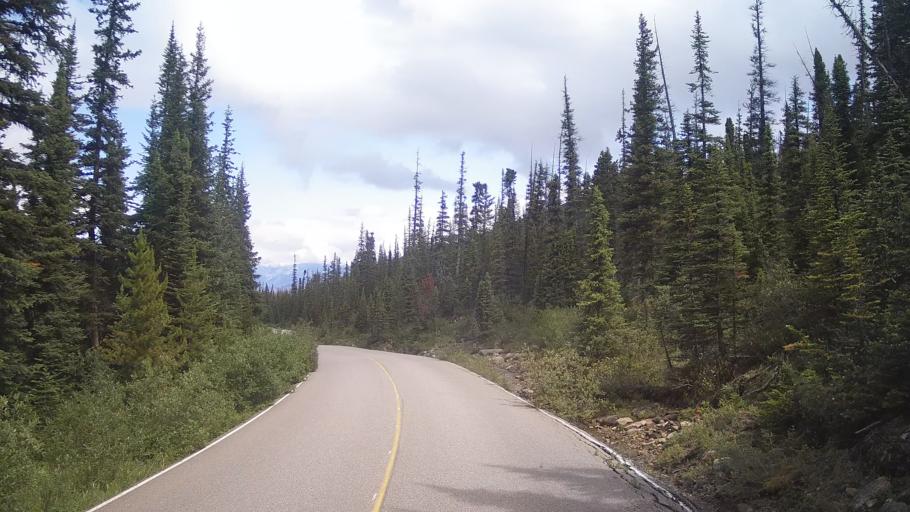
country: CA
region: Alberta
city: Jasper Park Lodge
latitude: 52.7087
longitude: -118.0566
